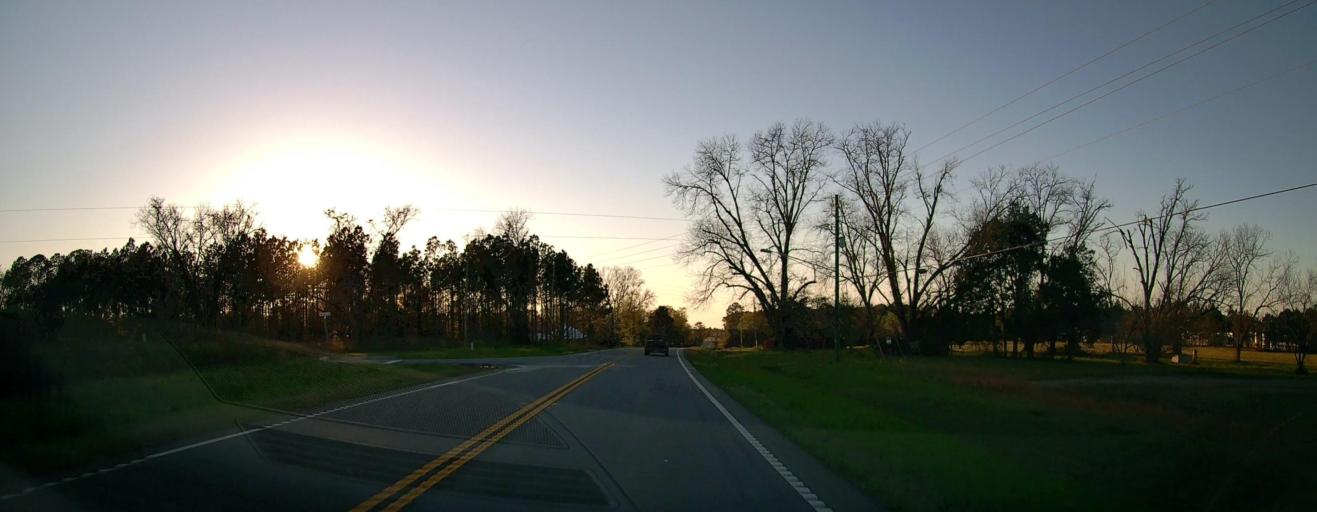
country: US
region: Georgia
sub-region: Crisp County
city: Cordele
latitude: 31.9507
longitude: -83.7146
